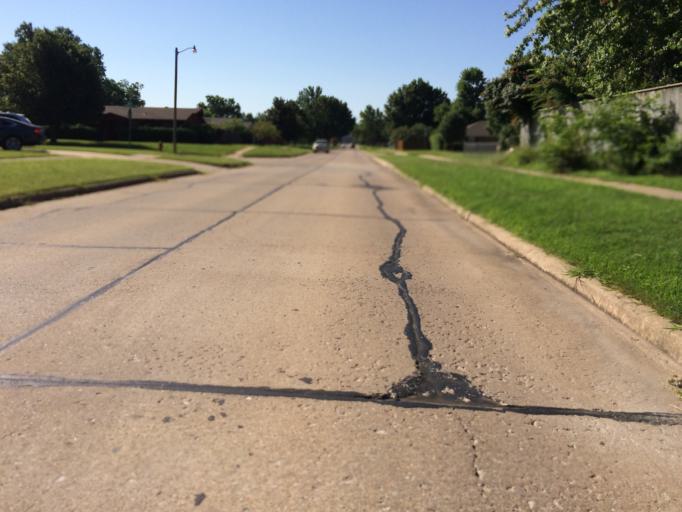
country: US
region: Oklahoma
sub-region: Cleveland County
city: Norman
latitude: 35.2315
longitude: -97.4645
